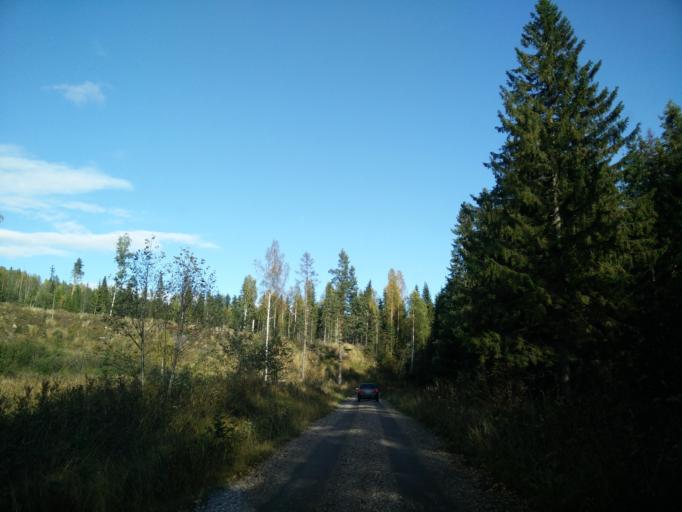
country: SE
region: Vaesternorrland
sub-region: Sundsvalls Kommun
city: Matfors
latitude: 62.3302
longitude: 16.9115
